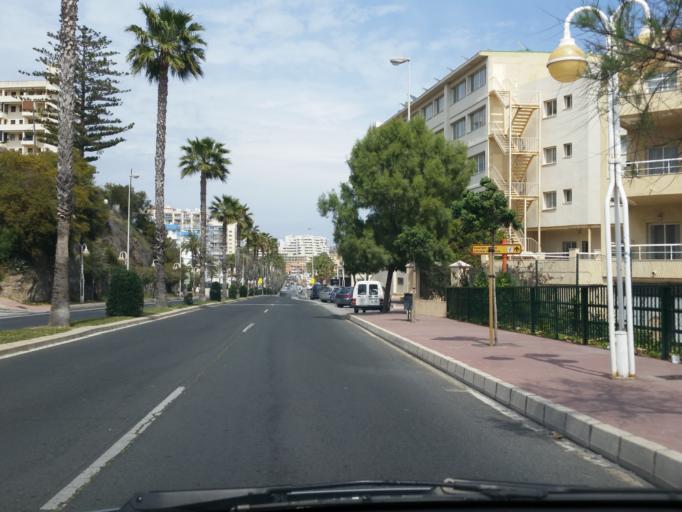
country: ES
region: Andalusia
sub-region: Provincia de Malaga
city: Benalmadena
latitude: 36.5841
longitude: -4.5346
